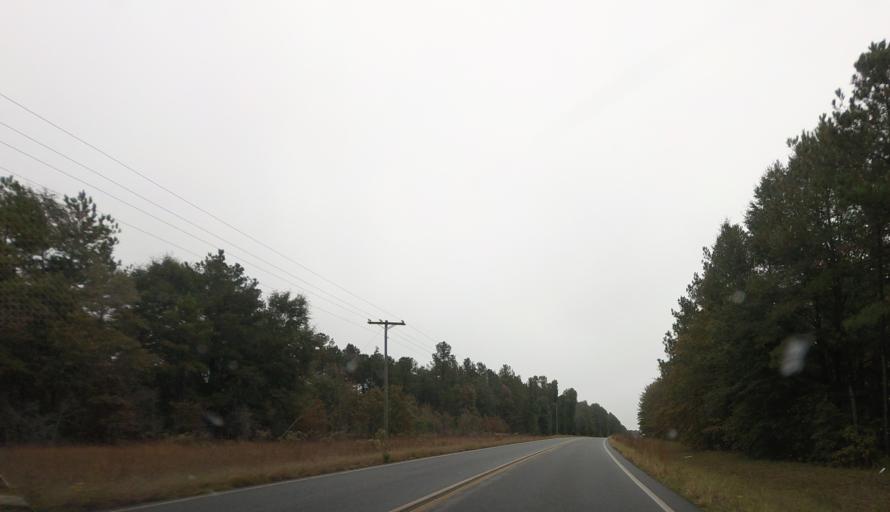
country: US
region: Georgia
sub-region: Marion County
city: Buena Vista
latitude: 32.3913
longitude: -84.4284
